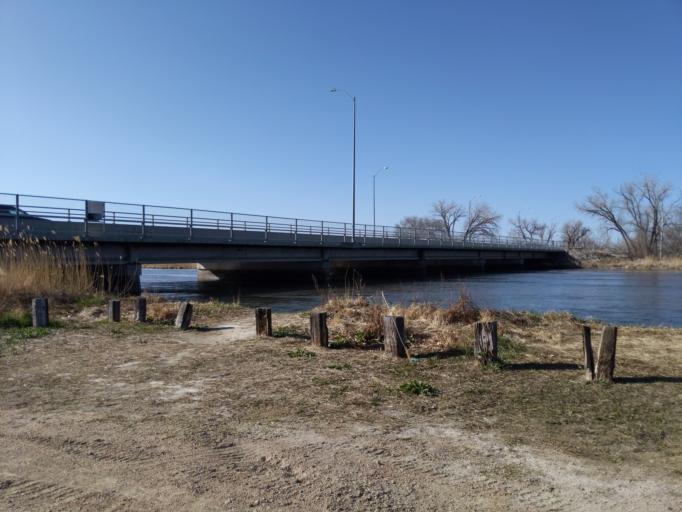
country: US
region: Nebraska
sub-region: Lincoln County
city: North Platte
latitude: 41.1540
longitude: -100.7588
